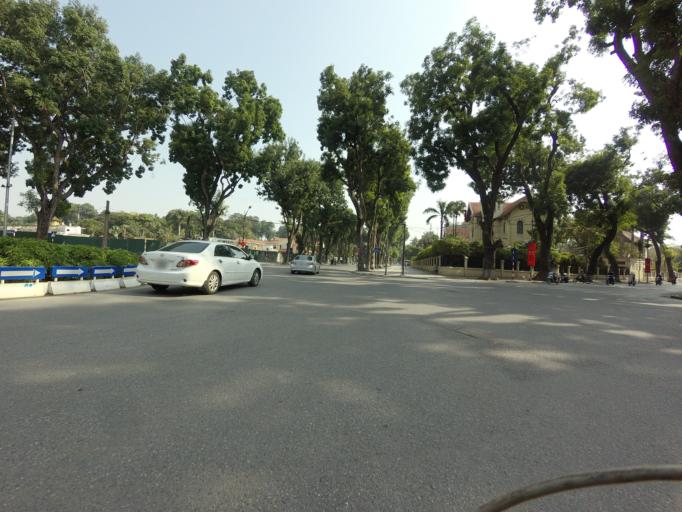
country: VN
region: Ha Noi
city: Hanoi
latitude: 21.0350
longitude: 105.8367
